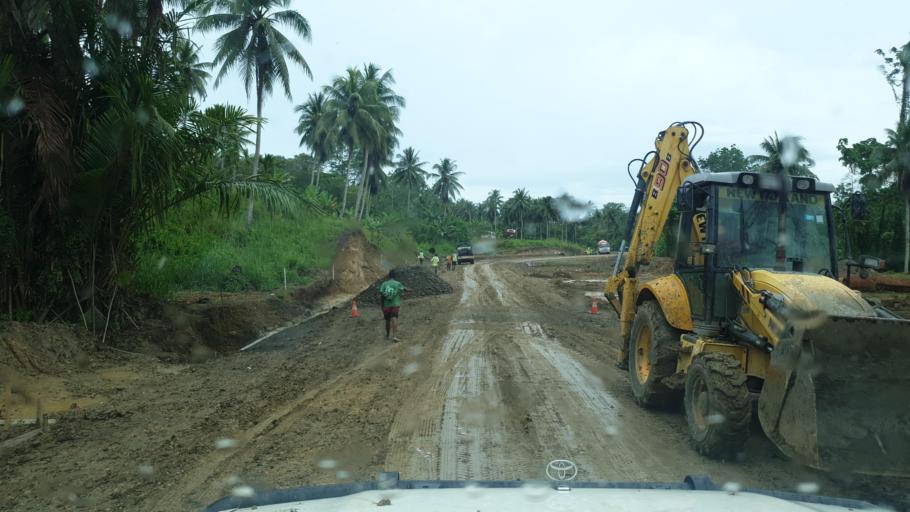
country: PG
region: Gulf
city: Kerema
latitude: -7.9975
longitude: 145.8242
